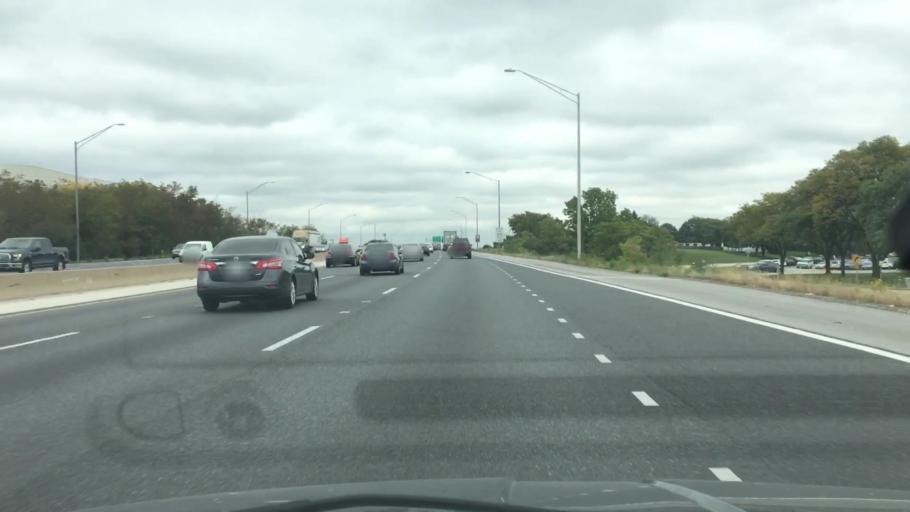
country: US
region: Illinois
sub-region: DuPage County
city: Burr Ridge
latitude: 41.7444
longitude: -87.9388
